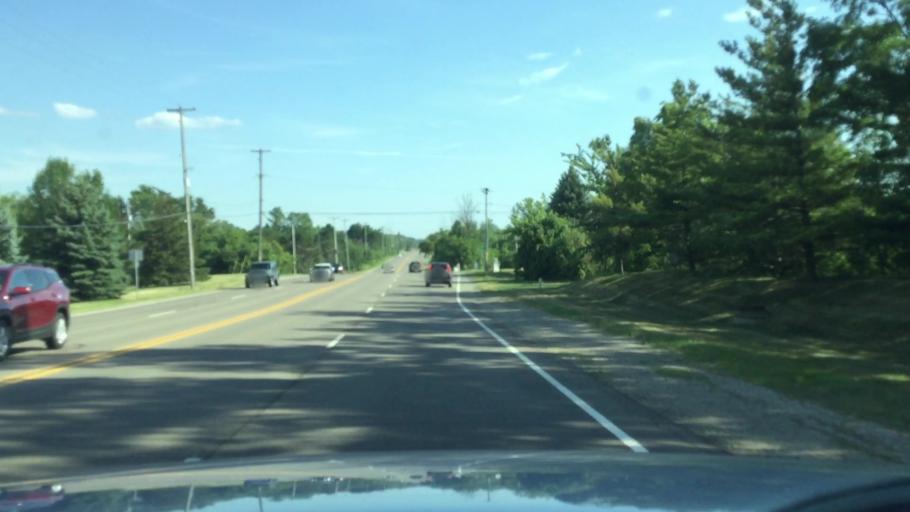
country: US
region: Michigan
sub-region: Genesee County
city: Grand Blanc
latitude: 42.8951
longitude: -83.6010
